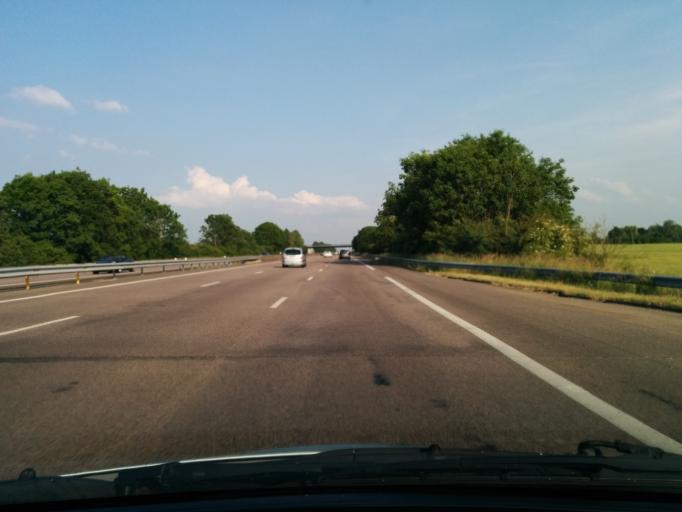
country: FR
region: Haute-Normandie
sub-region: Departement de l'Eure
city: La Chapelle-Reanville
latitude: 49.0758
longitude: 1.3964
